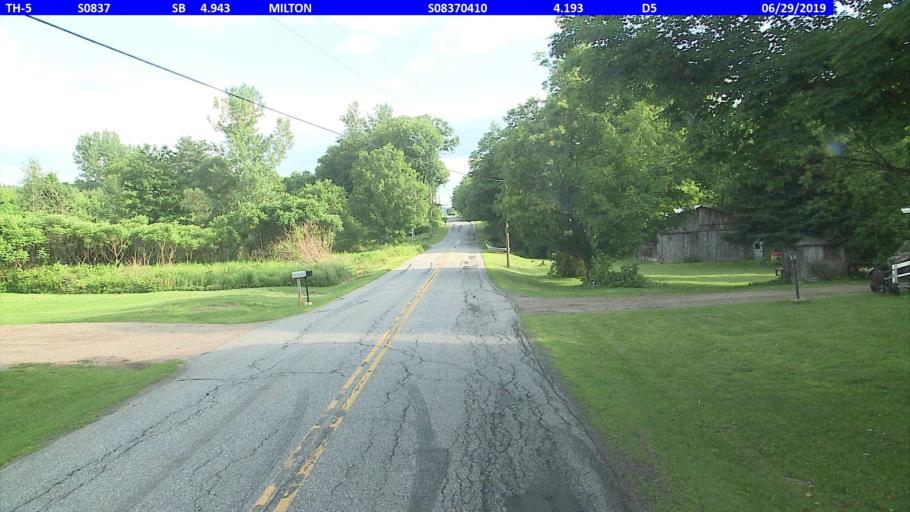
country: US
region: Vermont
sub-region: Chittenden County
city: Milton
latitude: 44.6329
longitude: -73.1013
